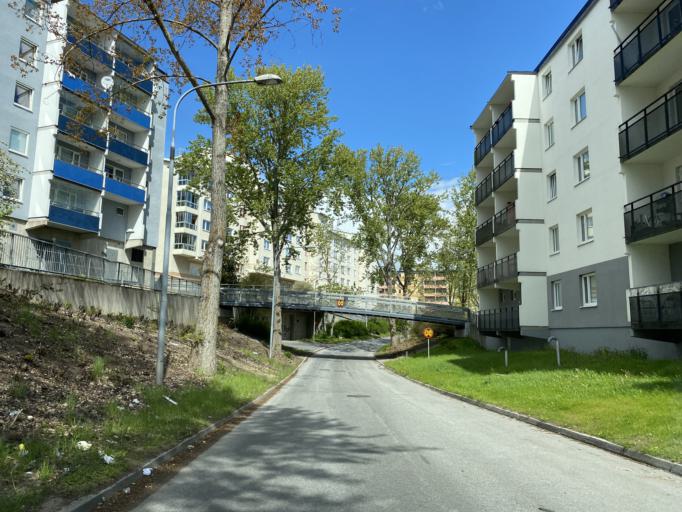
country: SE
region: Stockholm
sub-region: Stockholms Kommun
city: Kista
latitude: 59.4062
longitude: 17.9312
